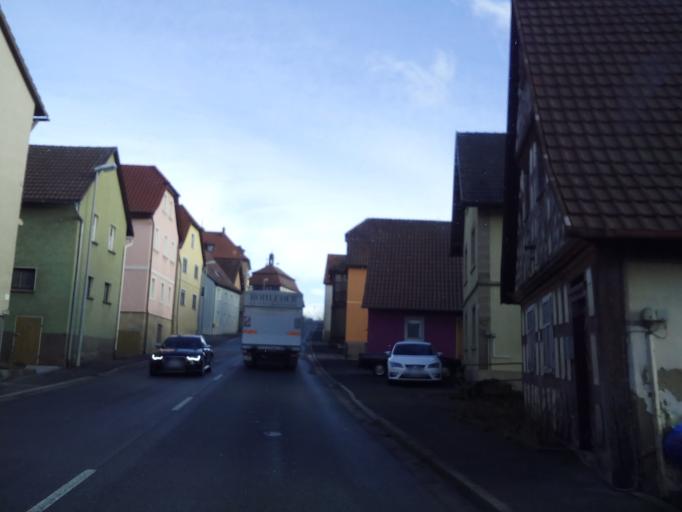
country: DE
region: Bavaria
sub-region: Upper Franconia
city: Mainleus
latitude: 50.1223
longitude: 11.3194
